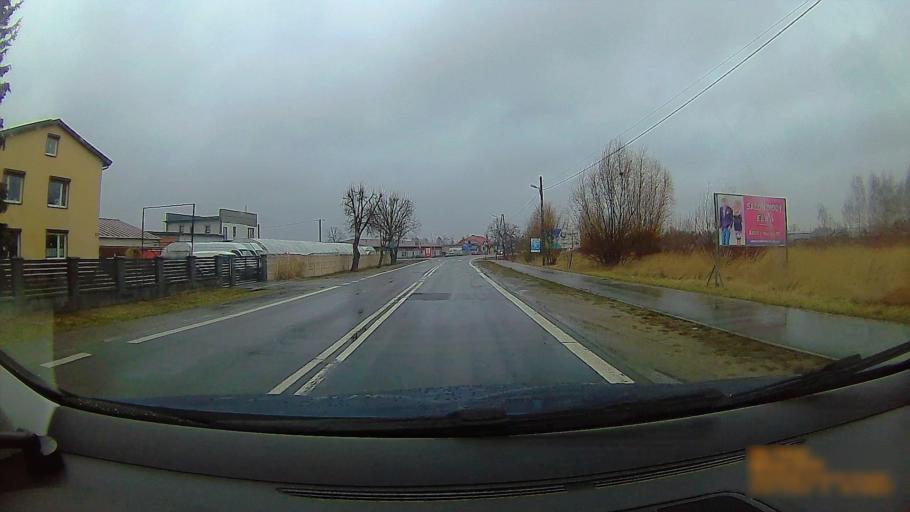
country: PL
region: Greater Poland Voivodeship
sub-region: Konin
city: Konin
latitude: 52.1894
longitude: 18.2653
